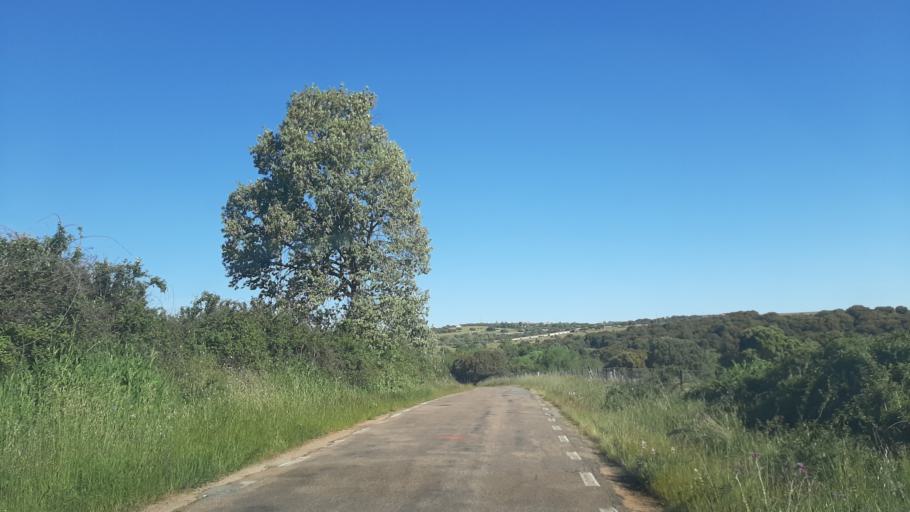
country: ES
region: Castille and Leon
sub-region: Provincia de Salamanca
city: Guijo de Avila
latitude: 40.5331
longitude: -5.6472
